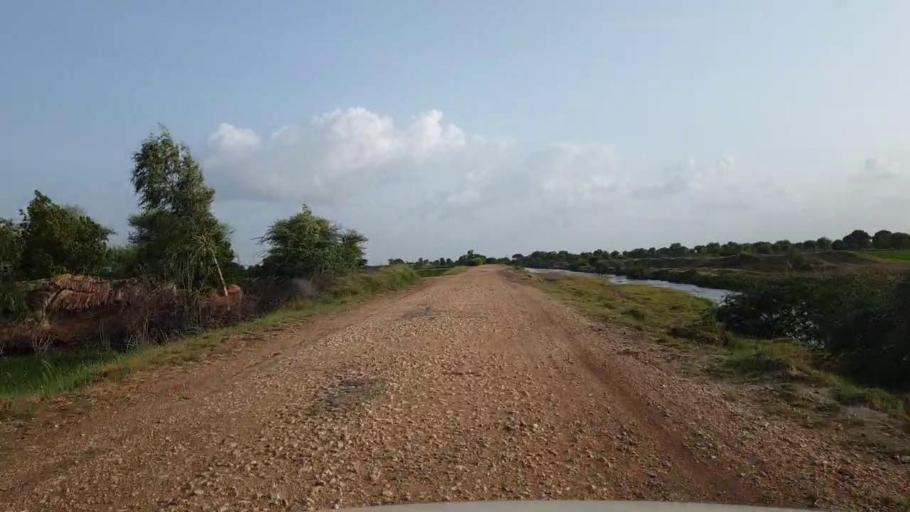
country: PK
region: Sindh
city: Kario
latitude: 24.8296
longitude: 68.6500
